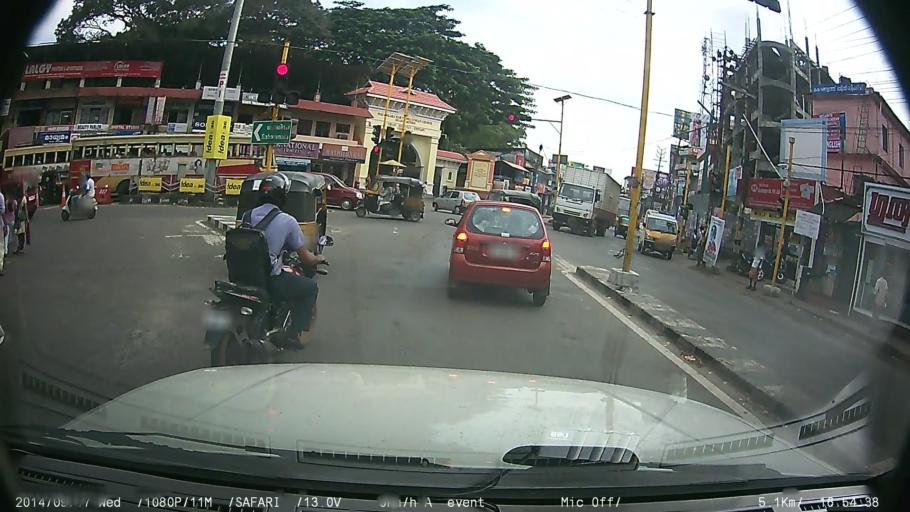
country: IN
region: Kerala
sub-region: Pattanamtitta
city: Tiruvalla
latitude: 9.3856
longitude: 76.5751
